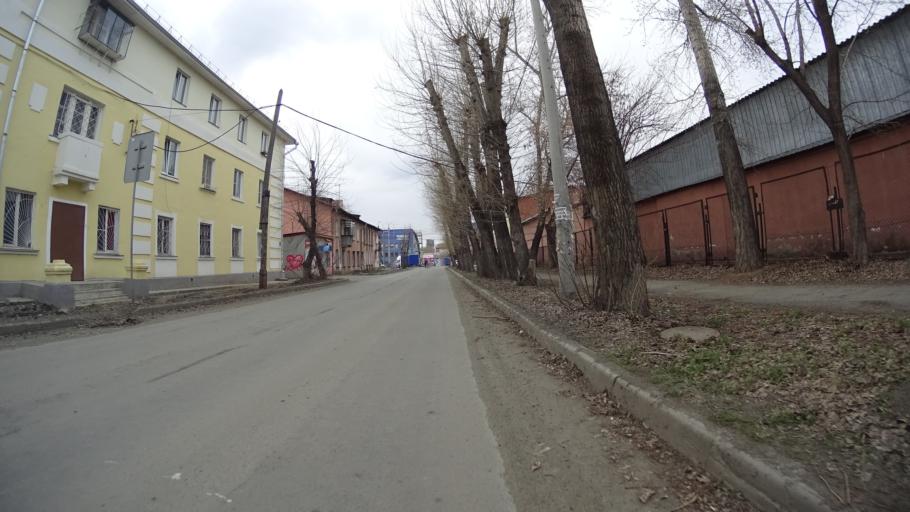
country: RU
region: Chelyabinsk
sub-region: Gorod Chelyabinsk
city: Chelyabinsk
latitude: 55.1657
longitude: 61.4360
